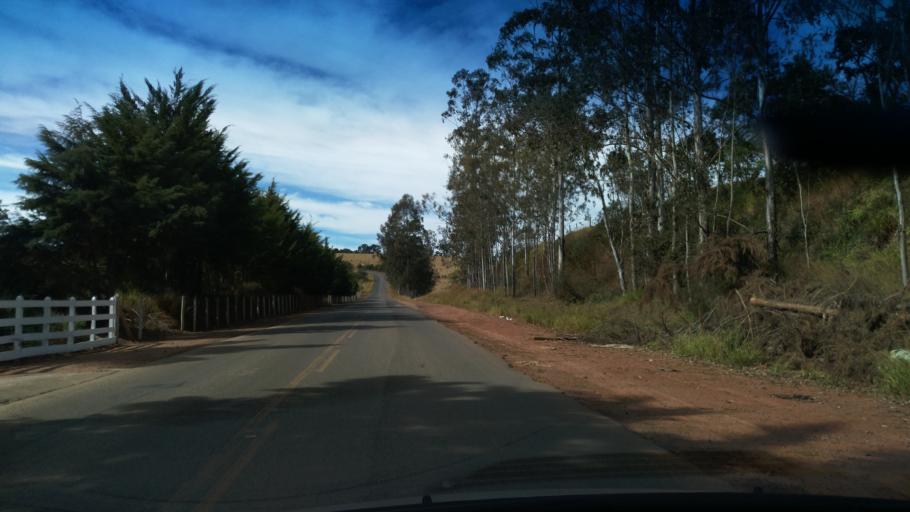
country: BR
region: Minas Gerais
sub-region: Andradas
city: Andradas
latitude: -22.0418
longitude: -46.3451
